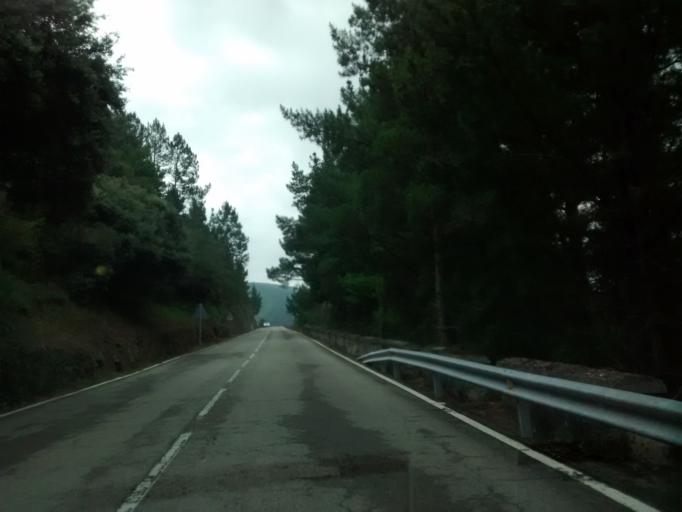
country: ES
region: Galicia
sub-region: Provincia de Ourense
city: Manzaneda
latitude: 42.3404
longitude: -7.2028
